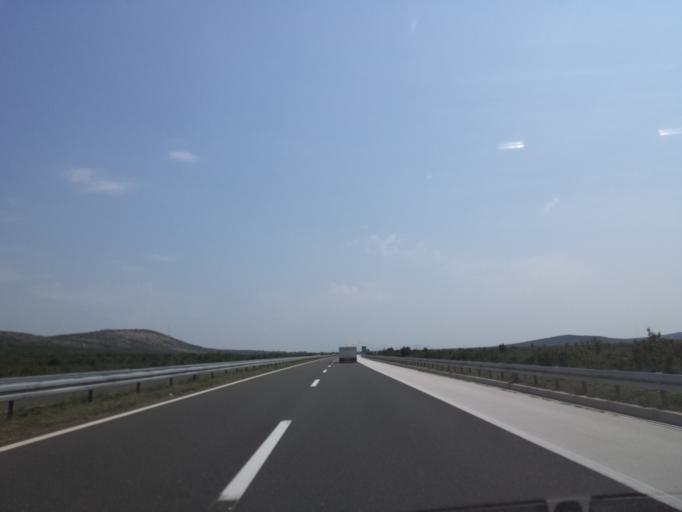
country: HR
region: Zadarska
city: Benkovac
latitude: 43.9508
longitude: 15.6857
